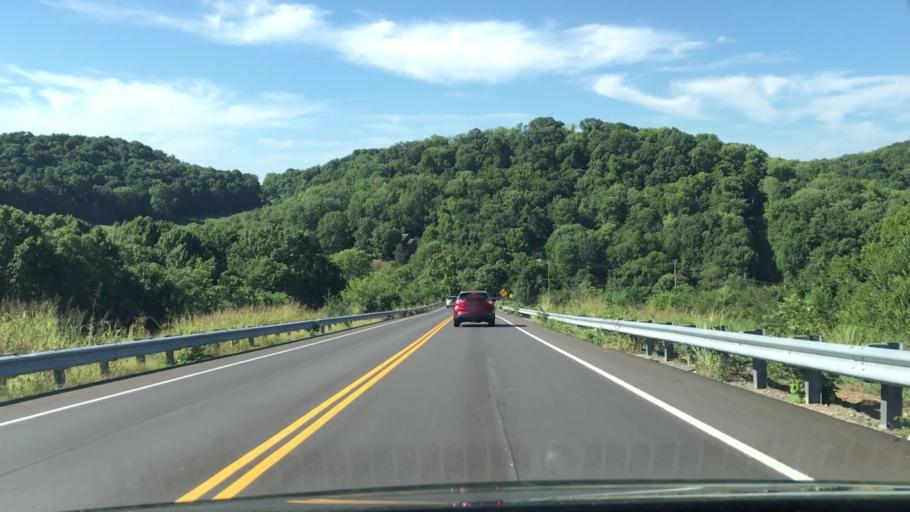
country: US
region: Tennessee
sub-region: Williamson County
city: Franklin
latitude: 35.9747
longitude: -86.8591
